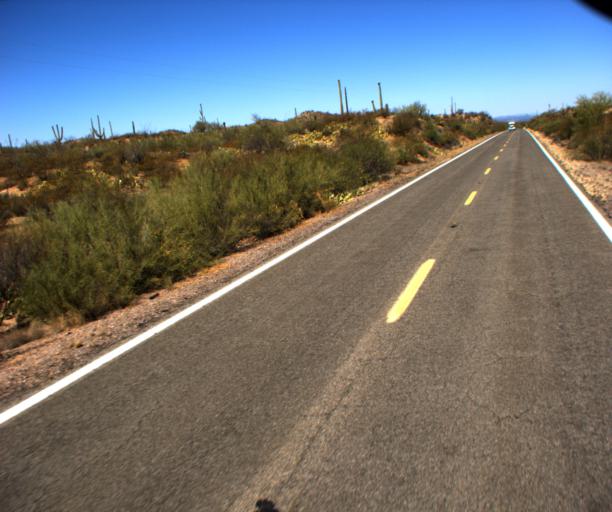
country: US
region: Arizona
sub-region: Pima County
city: Sells
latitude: 32.1745
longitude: -112.1754
